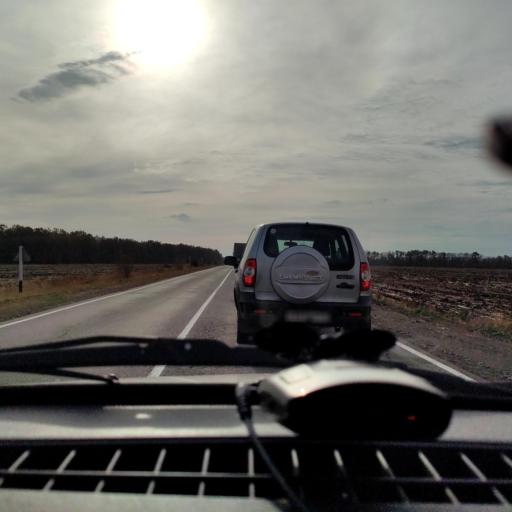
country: RU
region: Voronezj
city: Shilovo
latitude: 51.4481
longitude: 38.9920
